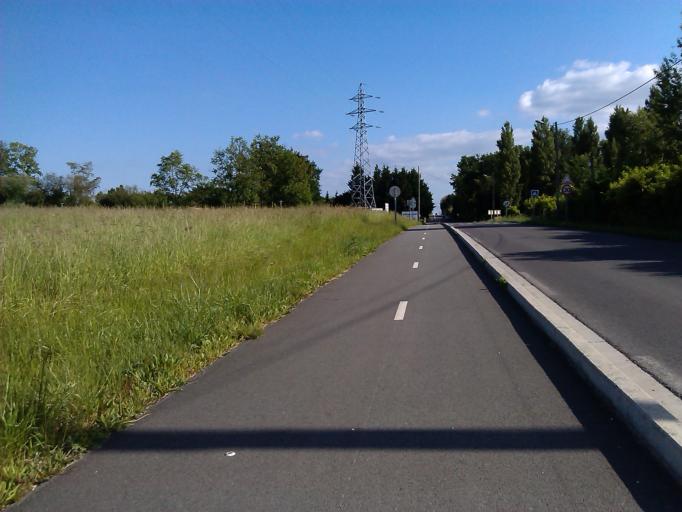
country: FR
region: Aquitaine
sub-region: Departement de la Gironde
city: Saint-Gervais
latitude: 45.0081
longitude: -0.4480
